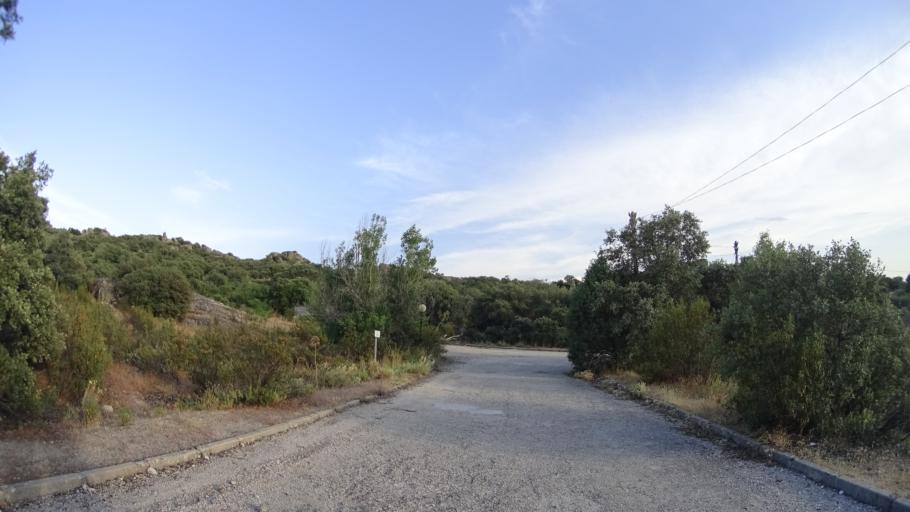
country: ES
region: Madrid
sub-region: Provincia de Madrid
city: Torrelodones
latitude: 40.5926
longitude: -3.9457
